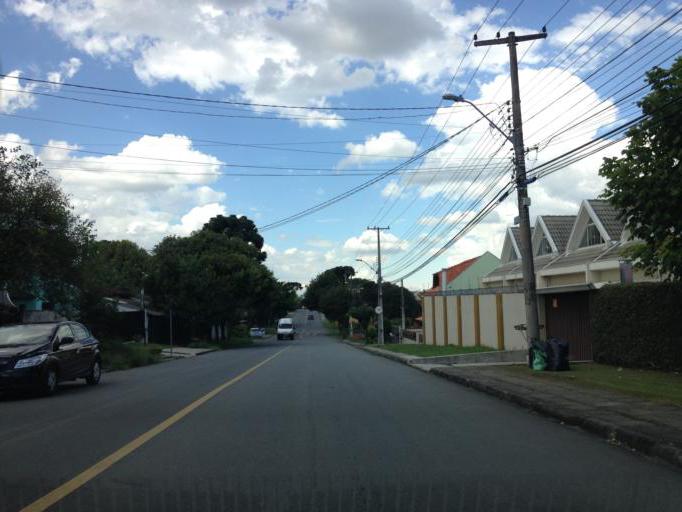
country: BR
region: Parana
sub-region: Curitiba
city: Curitiba
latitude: -25.4115
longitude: -49.2290
